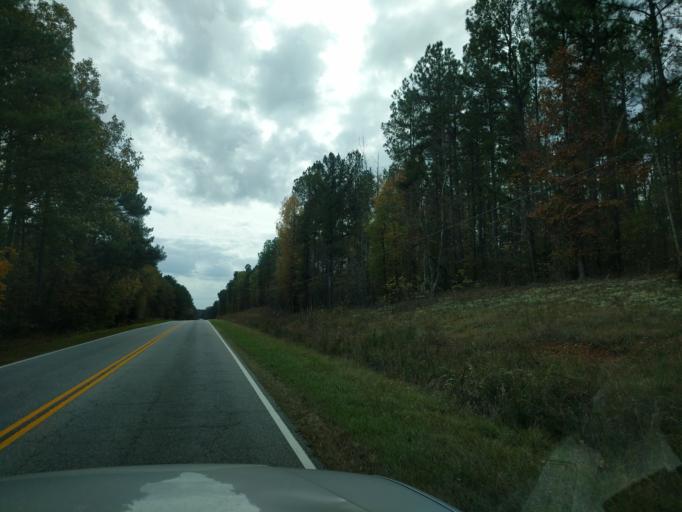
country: US
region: South Carolina
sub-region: Saluda County
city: Saluda
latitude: 34.1396
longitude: -81.8445
